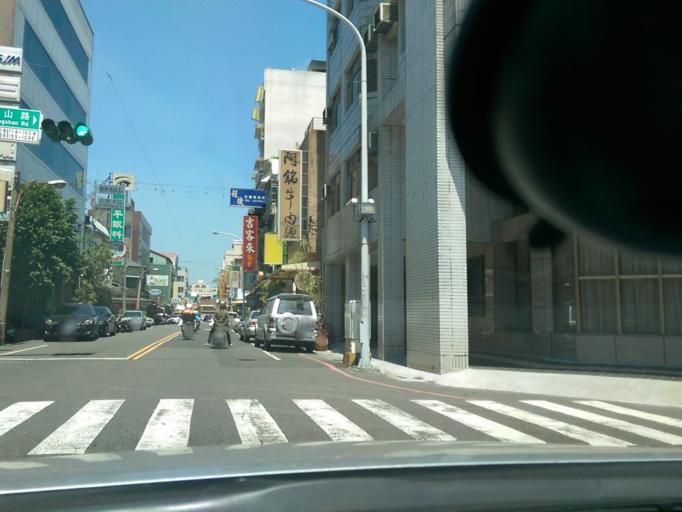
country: TW
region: Taiwan
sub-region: Chiayi
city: Jiayi Shi
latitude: 23.4819
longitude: 120.4561
